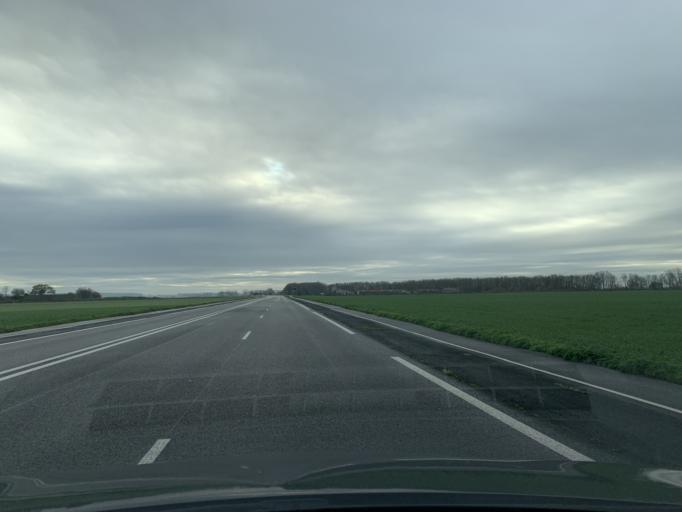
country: FR
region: Nord-Pas-de-Calais
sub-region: Departement du Nord
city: Goeulzin
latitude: 50.3338
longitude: 3.1029
